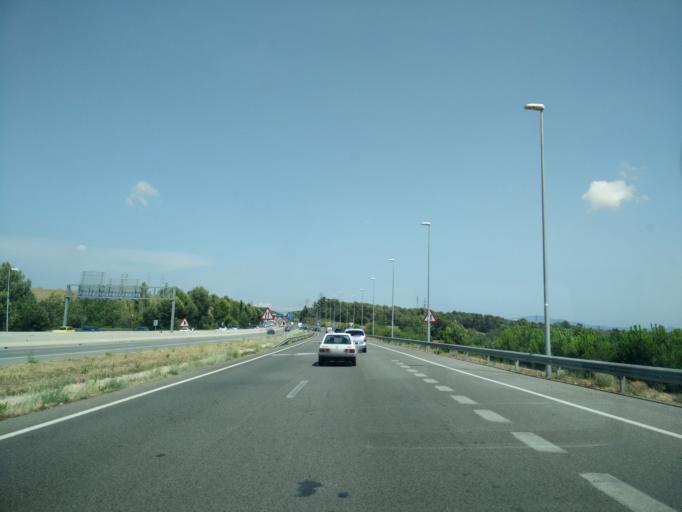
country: ES
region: Catalonia
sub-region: Provincia de Barcelona
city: Sant Quirze del Valles
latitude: 41.5421
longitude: 2.0535
